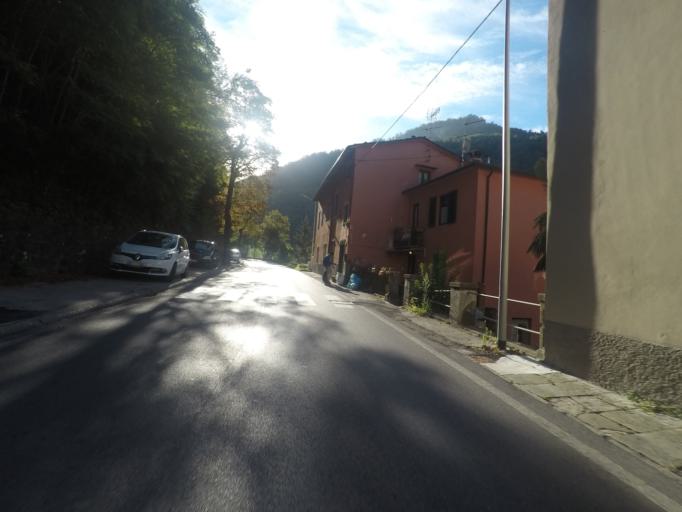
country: IT
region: Tuscany
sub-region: Provincia di Lucca
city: Bagni di Lucca
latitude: 44.0042
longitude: 10.5809
